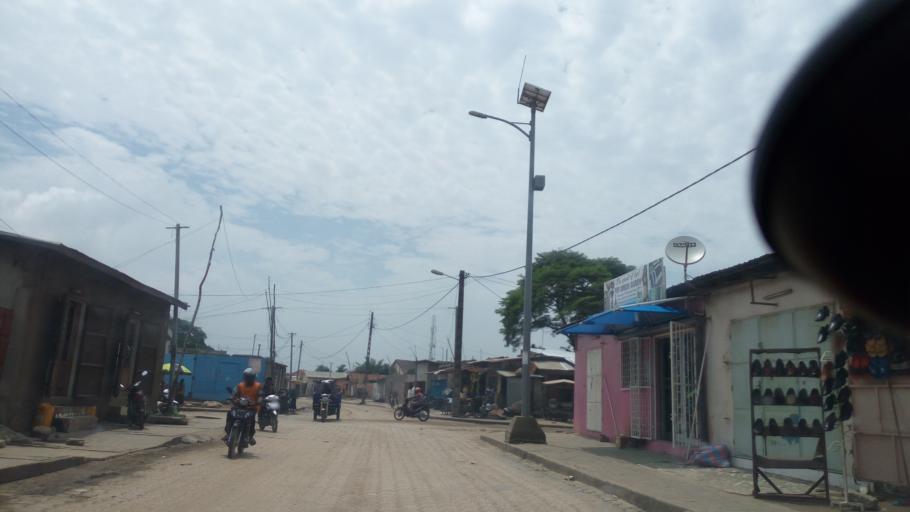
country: BJ
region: Atlantique
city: Abomey-Calavi
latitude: 6.3875
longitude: 2.3441
